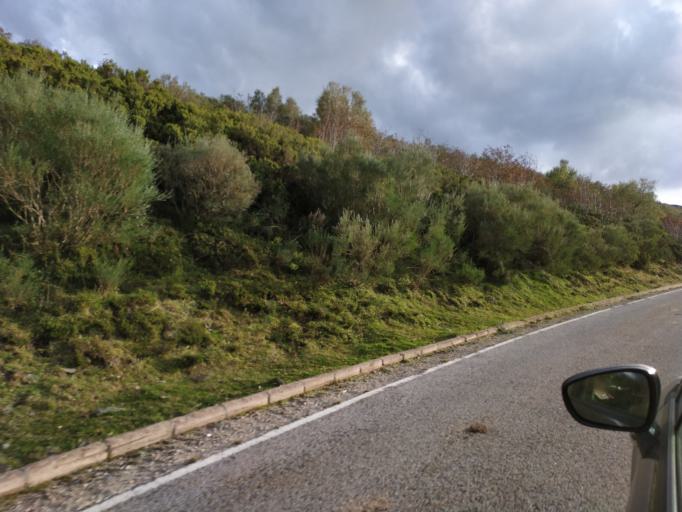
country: ES
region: Castille and Leon
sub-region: Provincia de Leon
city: Candin
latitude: 42.8696
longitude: -6.8202
